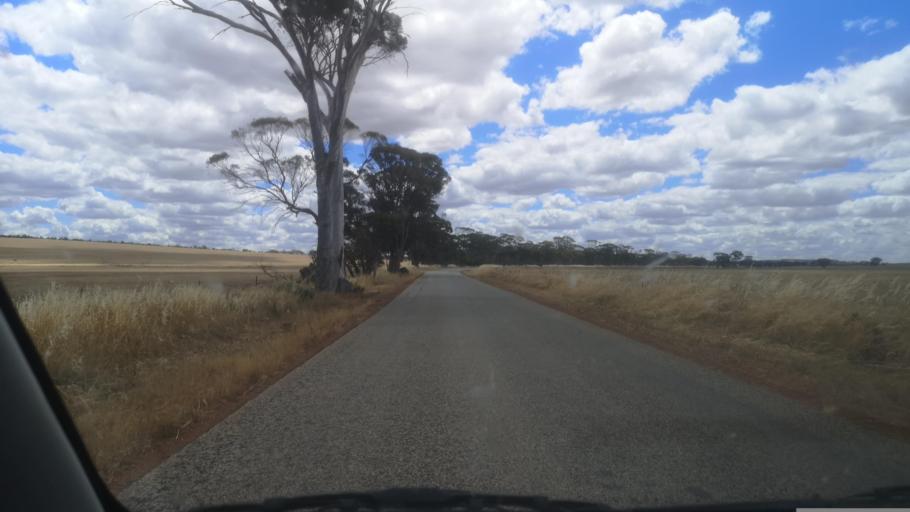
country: AU
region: Western Australia
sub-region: Cunderdin
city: Cunderdin
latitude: -32.0518
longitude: 117.4179
